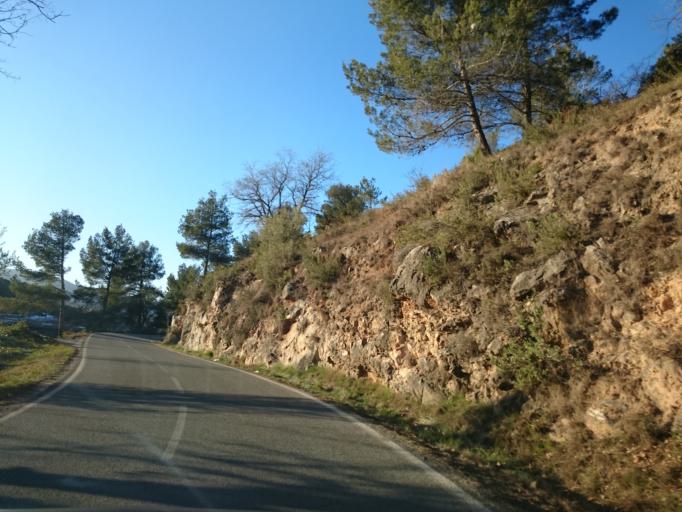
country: ES
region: Catalonia
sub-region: Provincia de Tarragona
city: la Bisbal del Penedes
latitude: 41.3690
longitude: 1.5017
